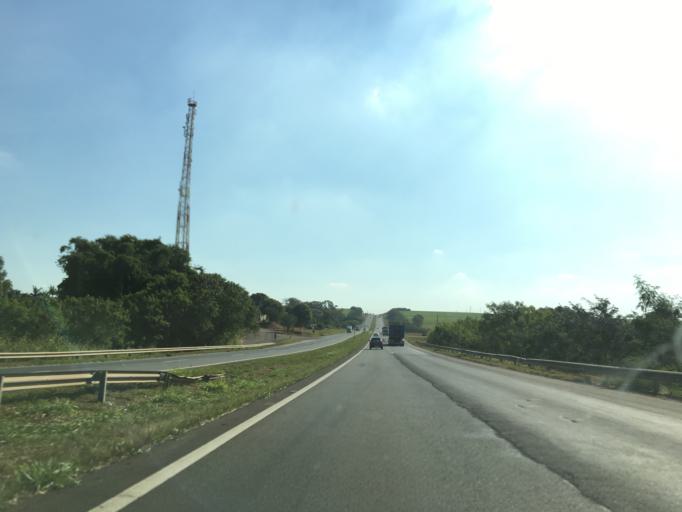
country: BR
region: Sao Paulo
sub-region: Piracicaba
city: Piracicaba
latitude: -22.7267
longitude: -47.5565
